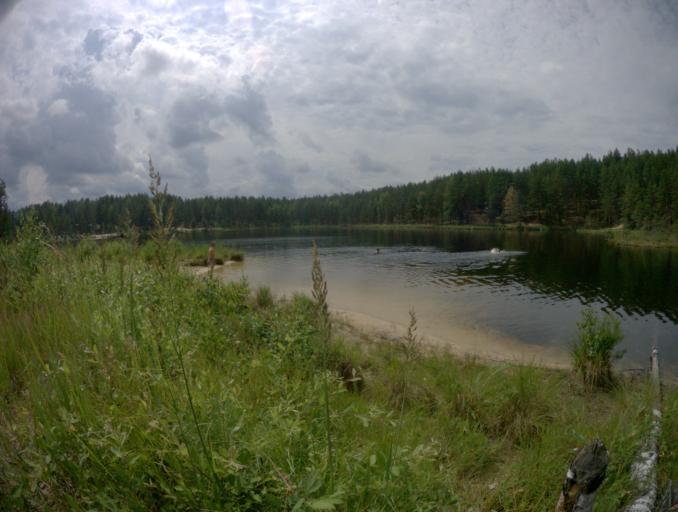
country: RU
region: Nizjnij Novgorod
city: Frolishchi
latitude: 56.3534
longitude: 42.7417
